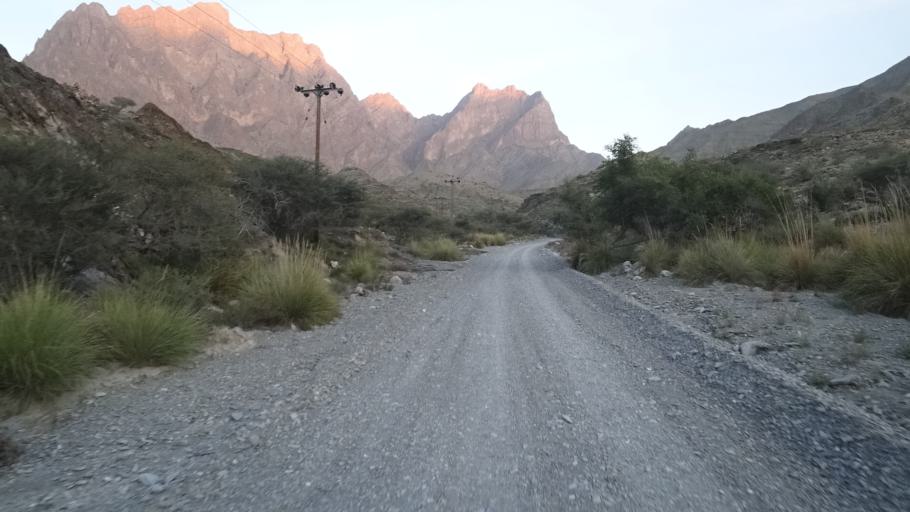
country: OM
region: Al Batinah
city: Bayt al `Awabi
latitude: 23.2401
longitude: 57.4391
